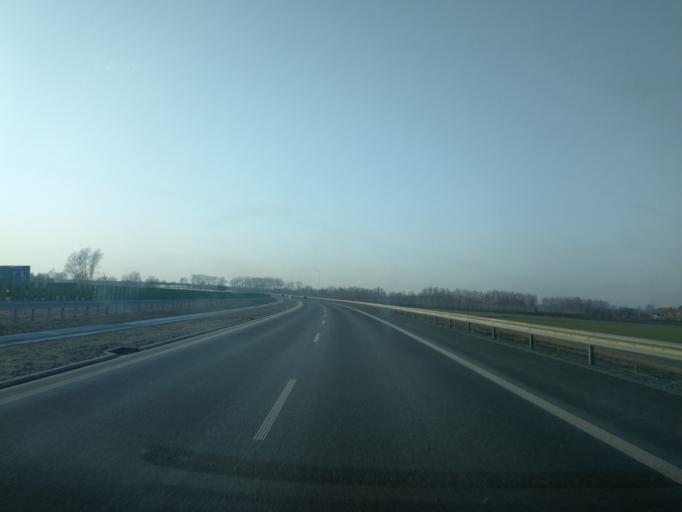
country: PL
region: Warmian-Masurian Voivodeship
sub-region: Powiat elblaski
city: Elblag
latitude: 54.1609
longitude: 19.3575
